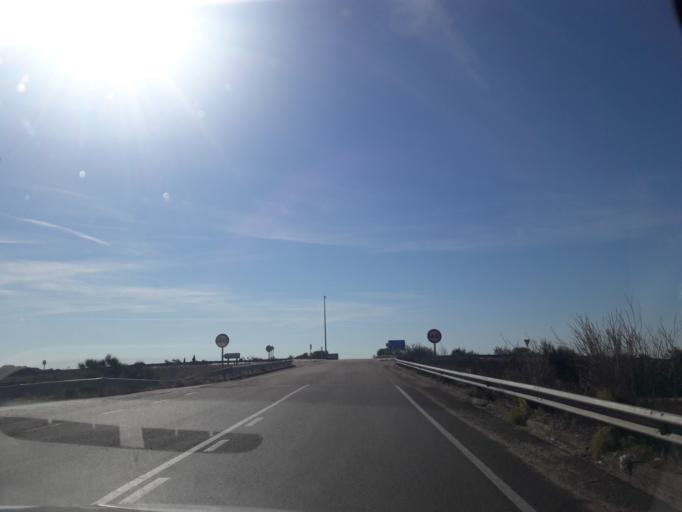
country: ES
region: Castille and Leon
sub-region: Provincia de Salamanca
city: Aldeanueva de Figueroa
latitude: 41.1375
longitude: -5.4890
